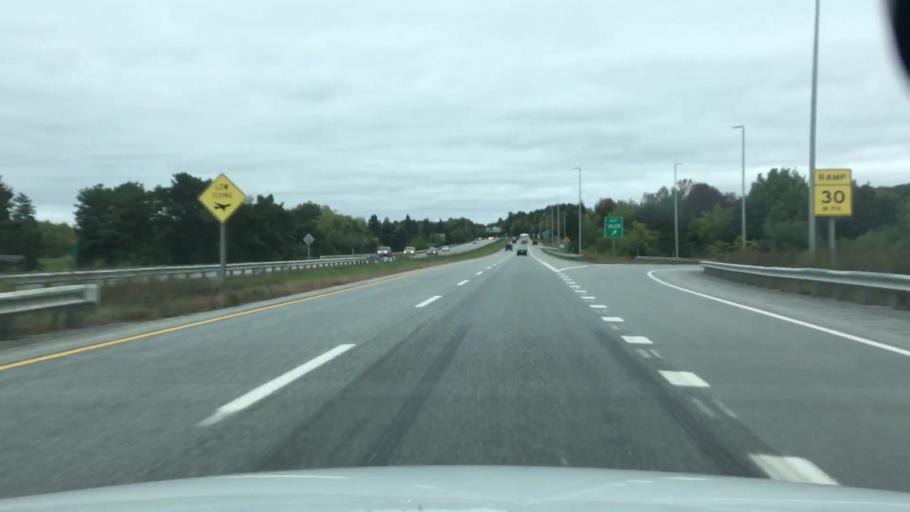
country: US
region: Maine
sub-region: Penobscot County
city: Bangor
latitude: 44.7876
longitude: -68.8077
